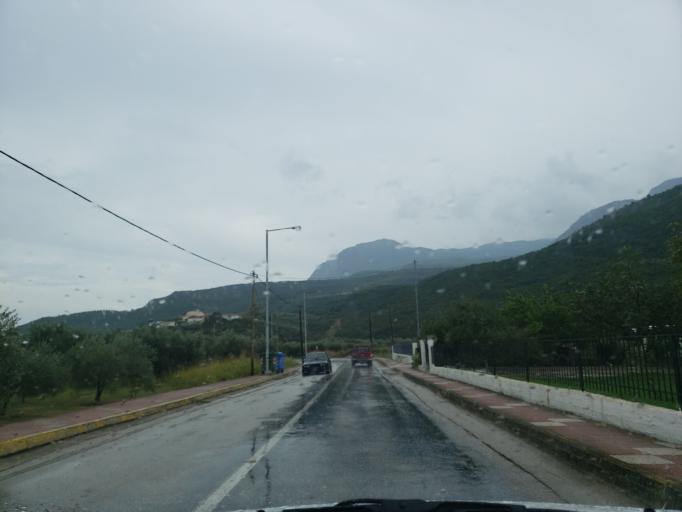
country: GR
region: Central Greece
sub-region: Nomos Fthiotidos
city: Anthili
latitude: 38.7993
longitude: 22.4717
